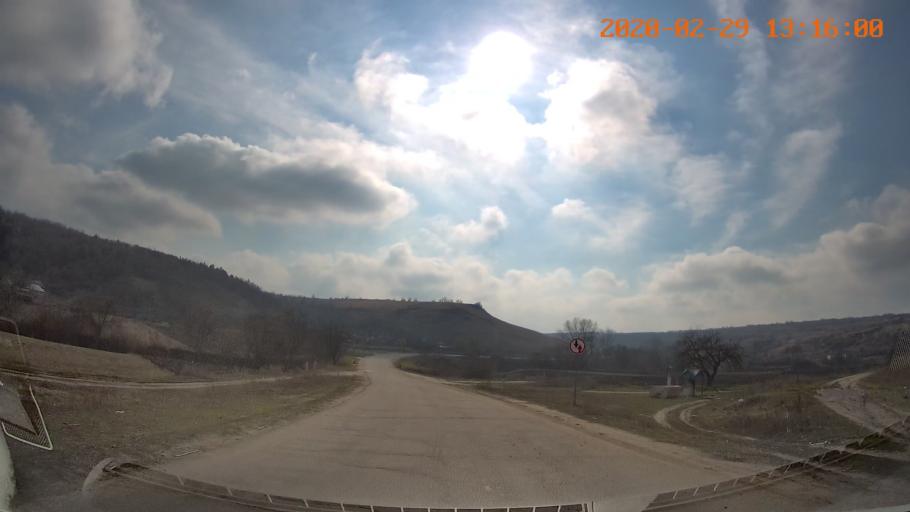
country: MD
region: Telenesti
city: Camenca
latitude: 48.0060
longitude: 28.6667
